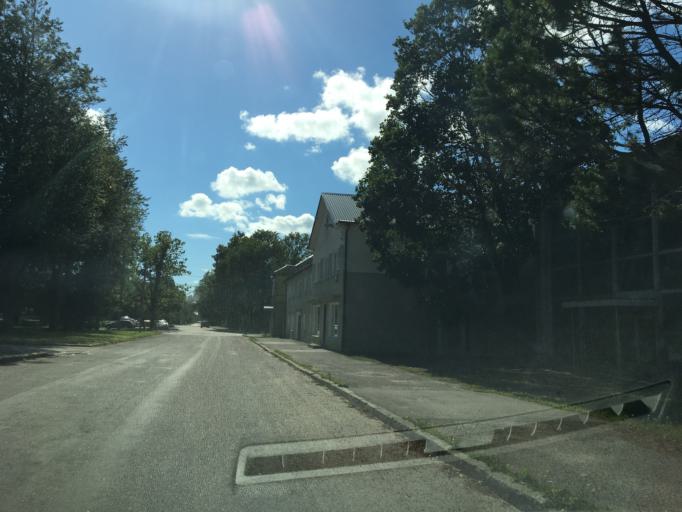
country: EE
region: Paernumaa
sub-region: Vaendra vald (alev)
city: Vandra
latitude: 58.6521
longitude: 25.0413
